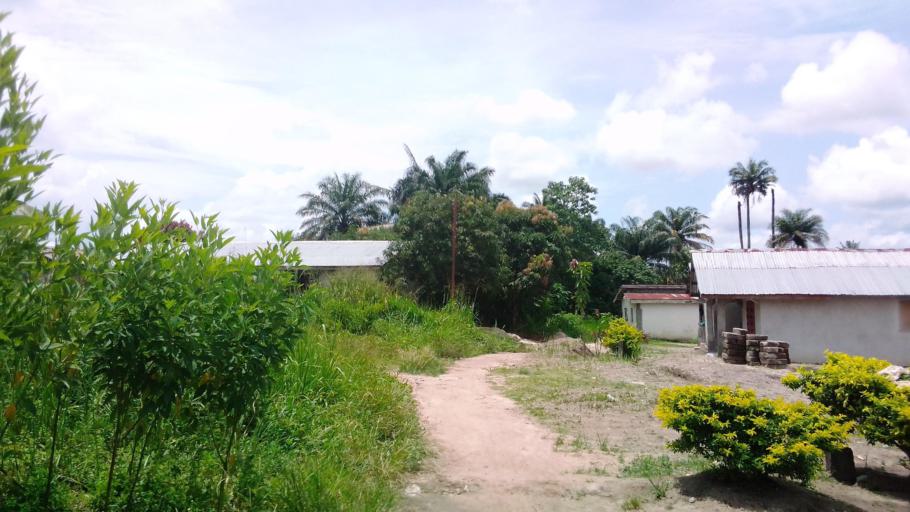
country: SL
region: Northern Province
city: Makeni
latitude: 8.8636
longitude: -12.0397
